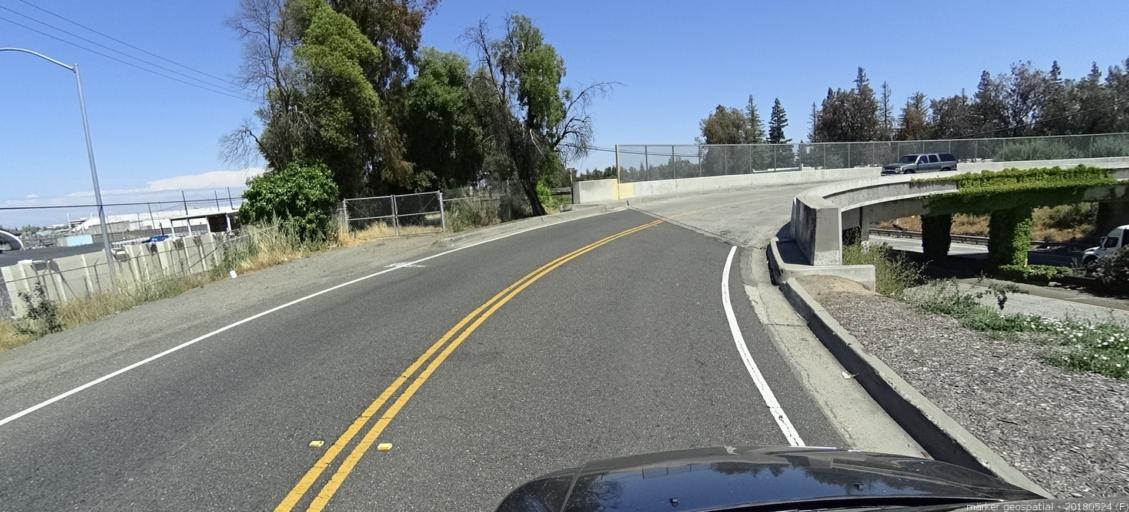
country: US
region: California
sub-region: Sacramento County
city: Sacramento
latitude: 38.6004
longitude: -121.4481
